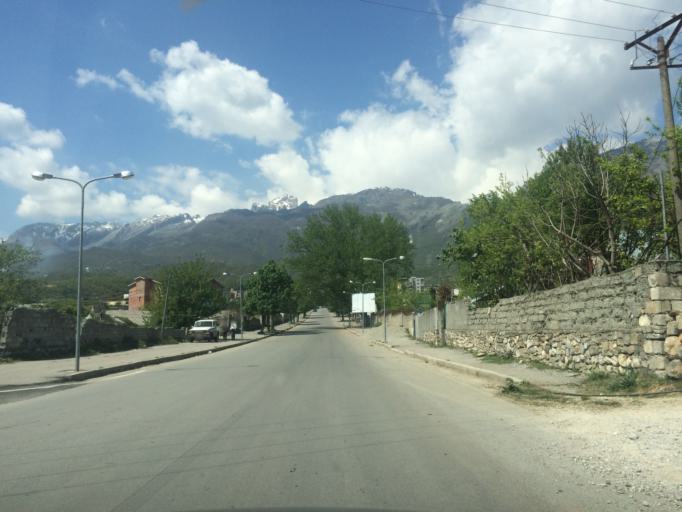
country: AL
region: Kukes
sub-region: Rrethi i Tropojes
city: Bajram Curri
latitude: 42.3570
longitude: 20.0835
